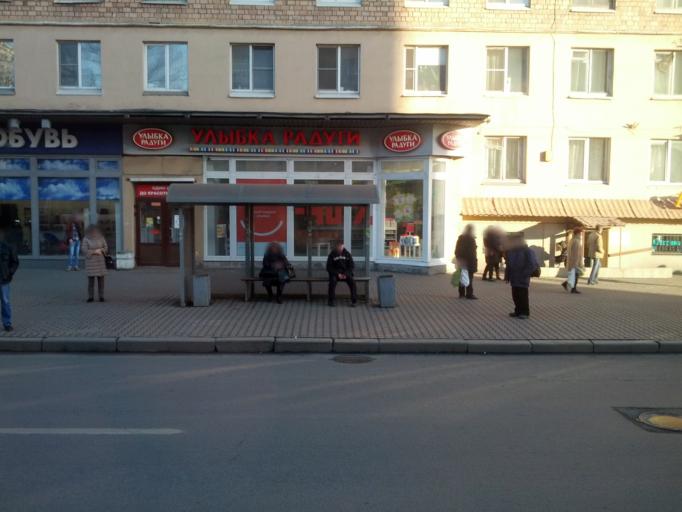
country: RU
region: St.-Petersburg
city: Centralniy
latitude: 59.9440
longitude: 30.4132
